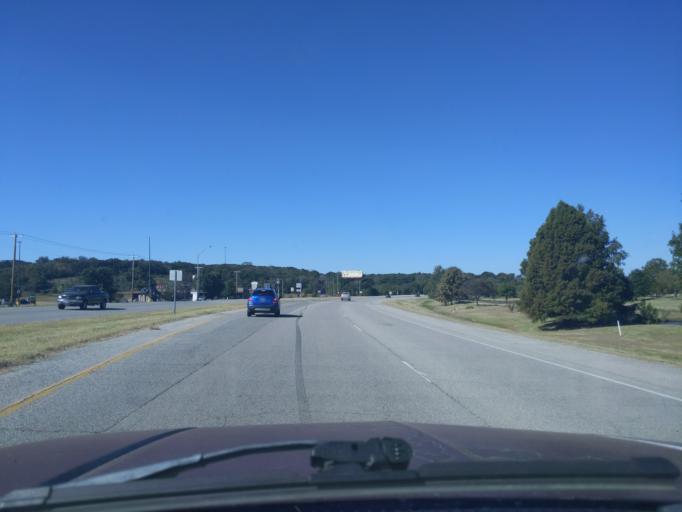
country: US
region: Oklahoma
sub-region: Creek County
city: Sapulpa
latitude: 35.9884
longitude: -96.1333
